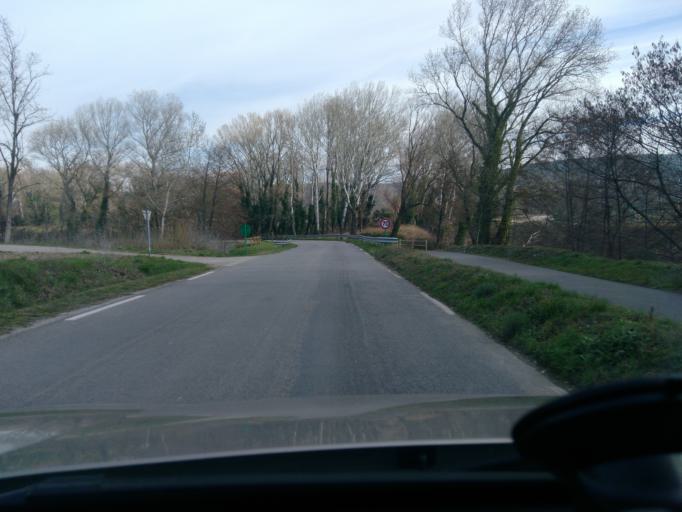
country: FR
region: Rhone-Alpes
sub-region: Departement de l'Ardeche
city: Cruas
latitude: 44.6391
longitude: 4.7609
